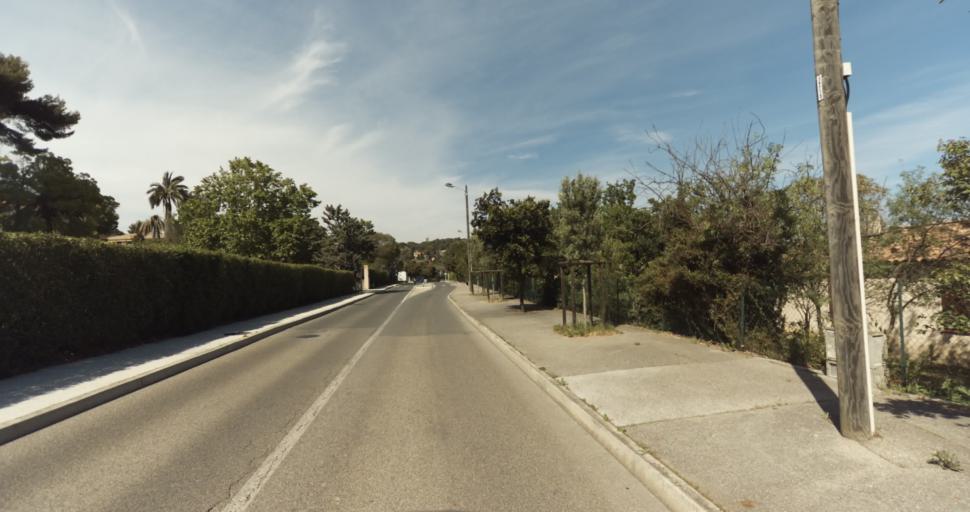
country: FR
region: Provence-Alpes-Cote d'Azur
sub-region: Departement du Var
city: Hyeres
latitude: 43.0900
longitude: 6.1220
